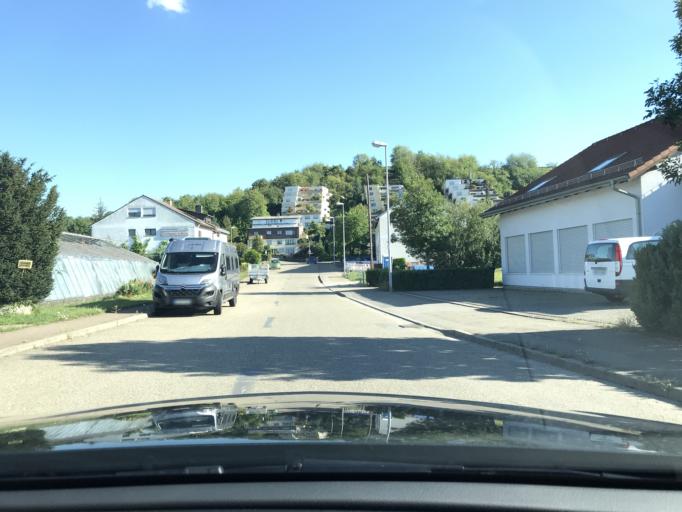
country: DE
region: Baden-Wuerttemberg
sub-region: Regierungsbezirk Stuttgart
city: Weinstadt-Endersbach
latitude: 48.7934
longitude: 9.3481
